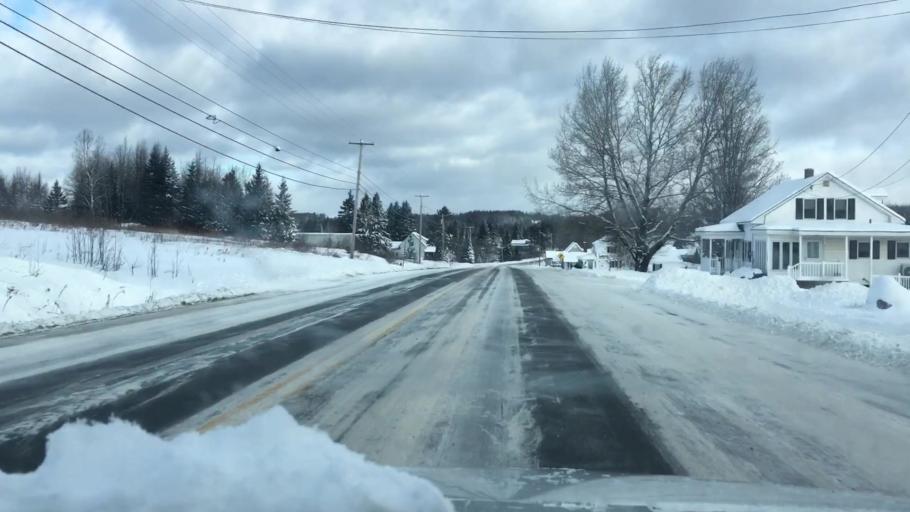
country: US
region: Maine
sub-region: Aroostook County
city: Caribou
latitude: 46.9748
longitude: -68.0357
